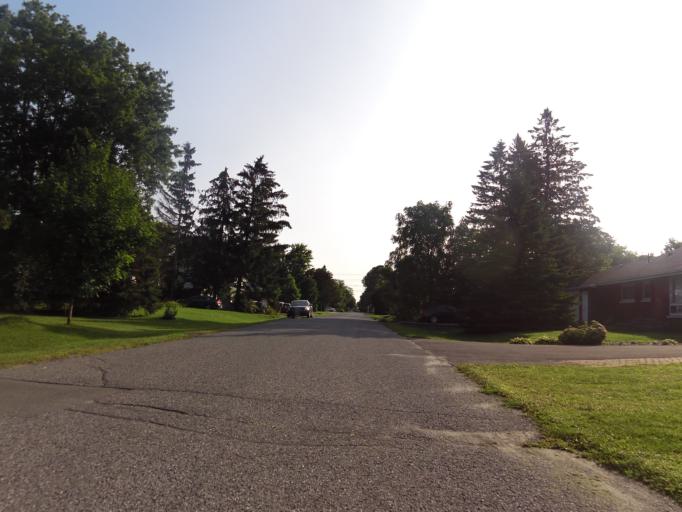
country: CA
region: Ontario
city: Ottawa
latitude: 45.3553
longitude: -75.7499
